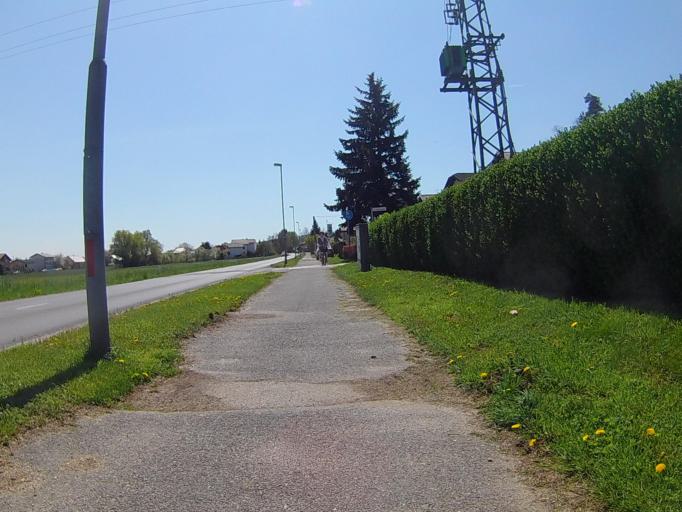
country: SI
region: Maribor
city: Razvanje
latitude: 46.5215
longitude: 15.6351
